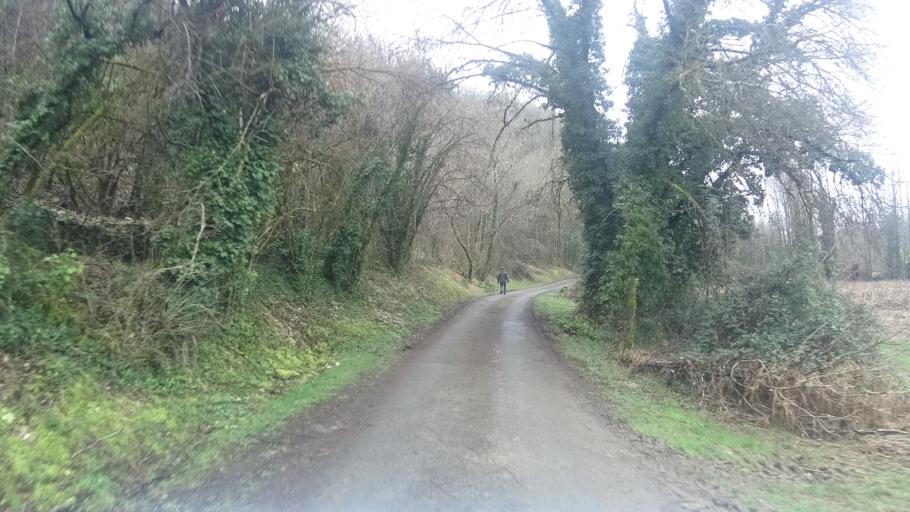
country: FR
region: Aquitaine
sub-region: Departement de la Dordogne
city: Terrasson-Lavilledieu
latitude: 45.1081
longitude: 1.2401
